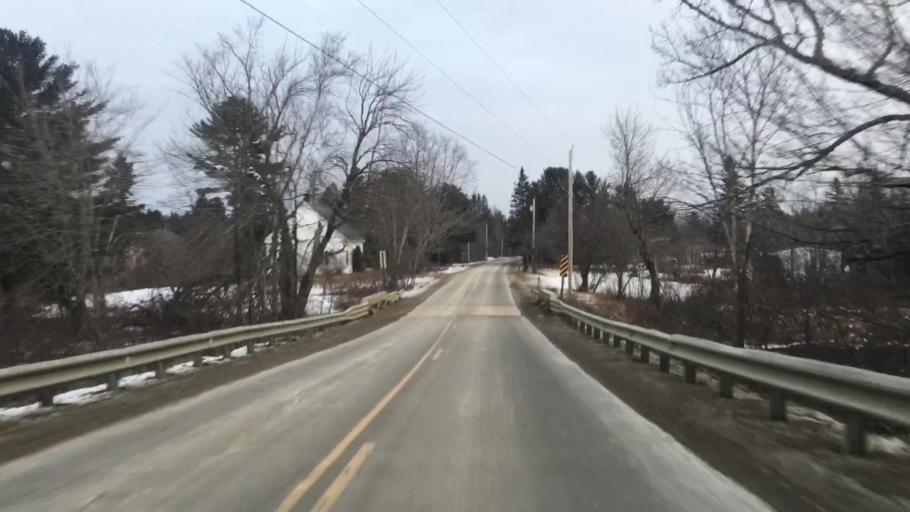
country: US
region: Maine
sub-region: Hancock County
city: Franklin
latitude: 44.6873
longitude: -68.3496
